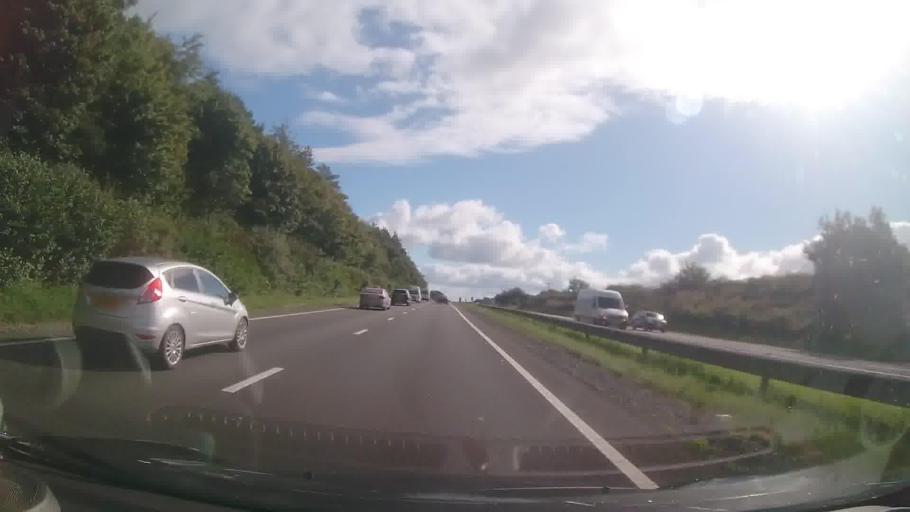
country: GB
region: Wales
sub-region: Carmarthenshire
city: Llanddarog
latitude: 51.8403
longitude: -4.2315
